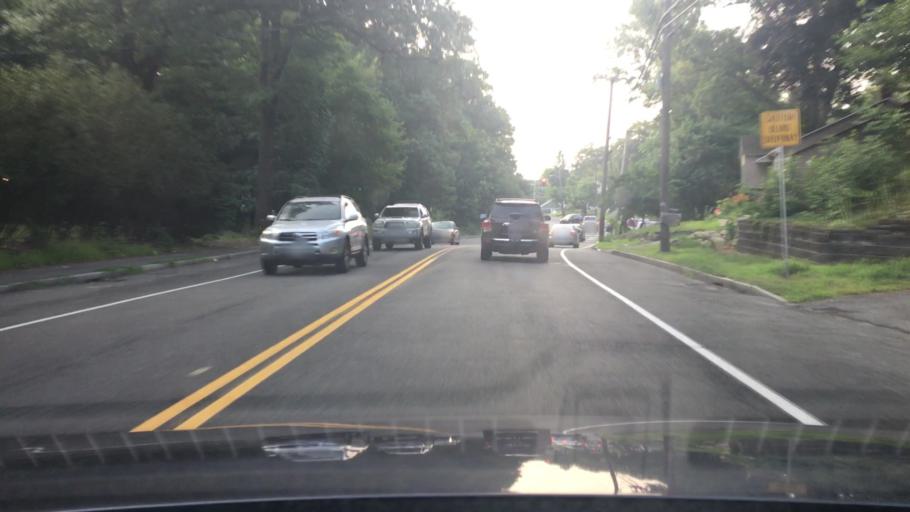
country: US
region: Massachusetts
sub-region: Essex County
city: Saugus
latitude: 42.4847
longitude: -71.0126
